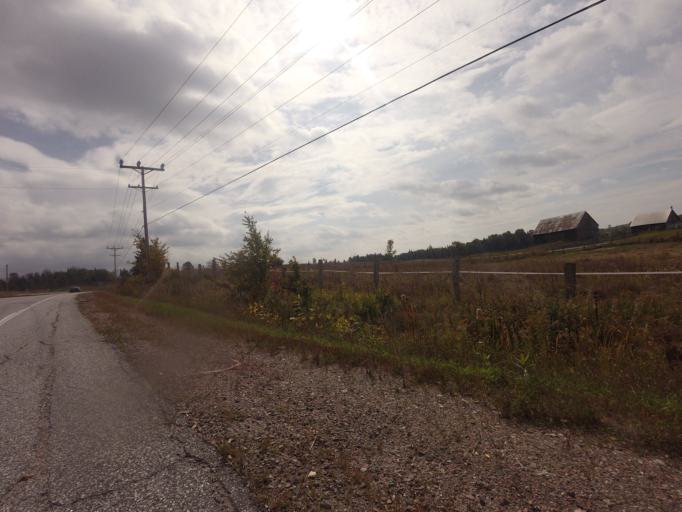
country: CA
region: Quebec
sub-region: Outaouais
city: Wakefield
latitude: 45.8610
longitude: -76.0120
